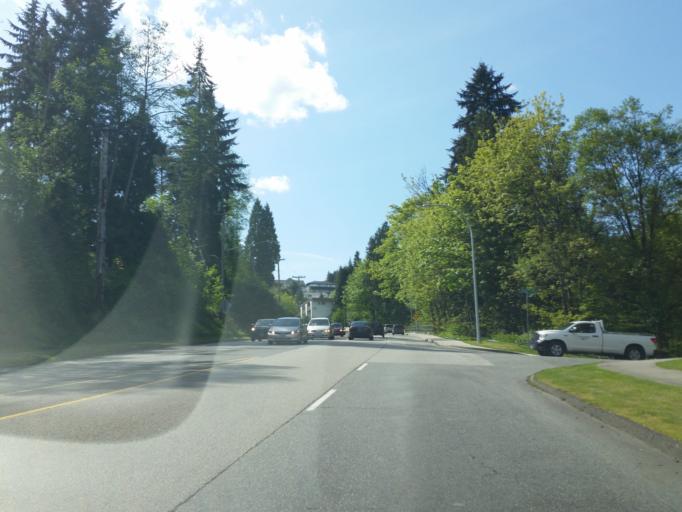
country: CA
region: British Columbia
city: Port Moody
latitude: 49.2744
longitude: -122.8718
